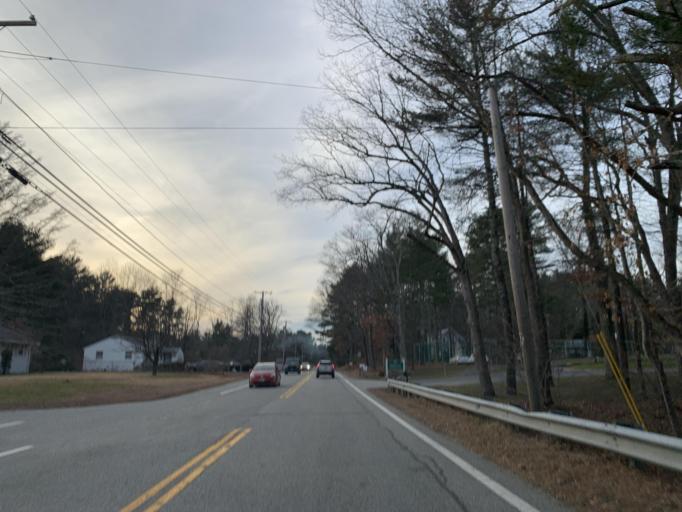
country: US
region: Rhode Island
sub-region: Providence County
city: Chepachet
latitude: 41.9052
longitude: -71.6507
